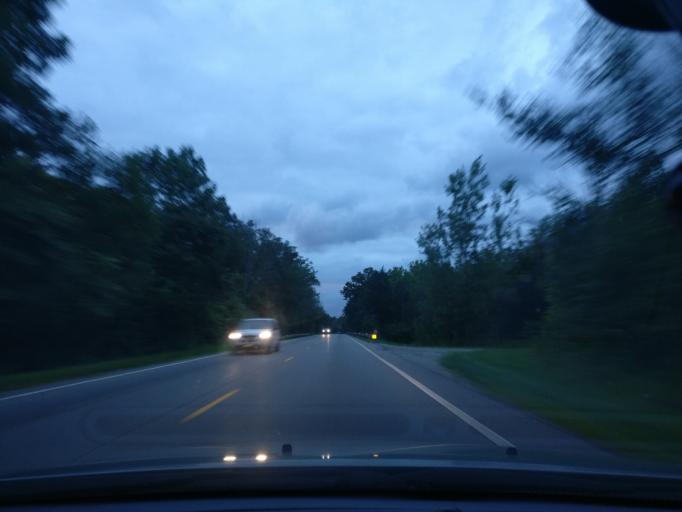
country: US
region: Ohio
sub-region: Warren County
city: Waynesville
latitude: 39.5340
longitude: -84.0980
